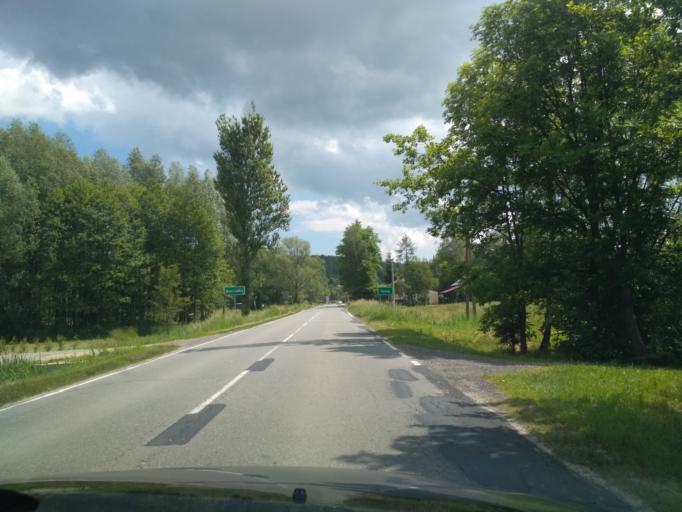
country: PL
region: Subcarpathian Voivodeship
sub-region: Powiat rzeszowski
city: Hyzne
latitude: 49.9282
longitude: 22.1504
